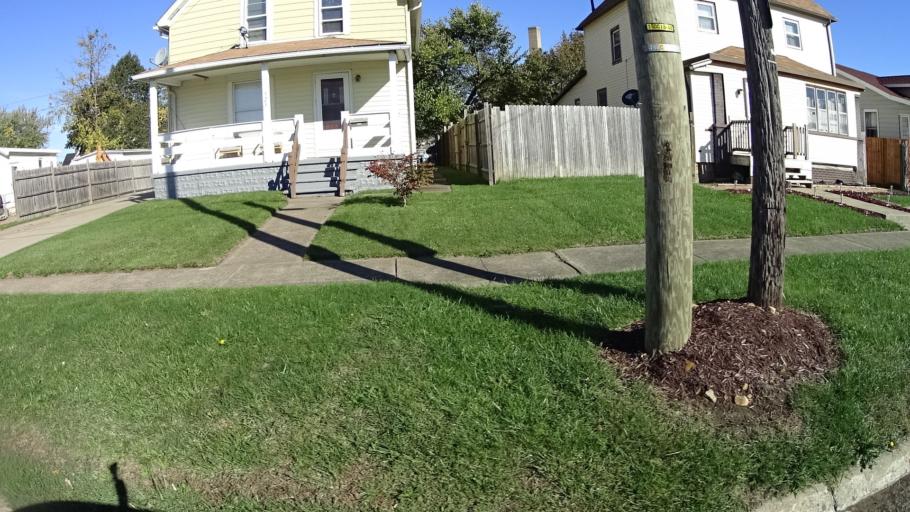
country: US
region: Ohio
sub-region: Lorain County
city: Lorain
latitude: 41.4388
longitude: -82.1625
